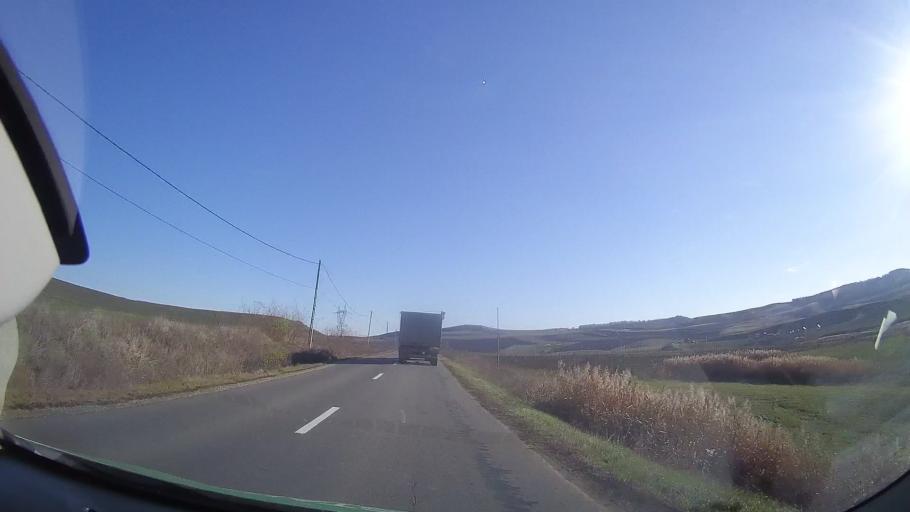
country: RO
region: Mures
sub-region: Comuna Mihesu de Campie
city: Mihesu de Campie
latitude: 46.6506
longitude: 24.1595
